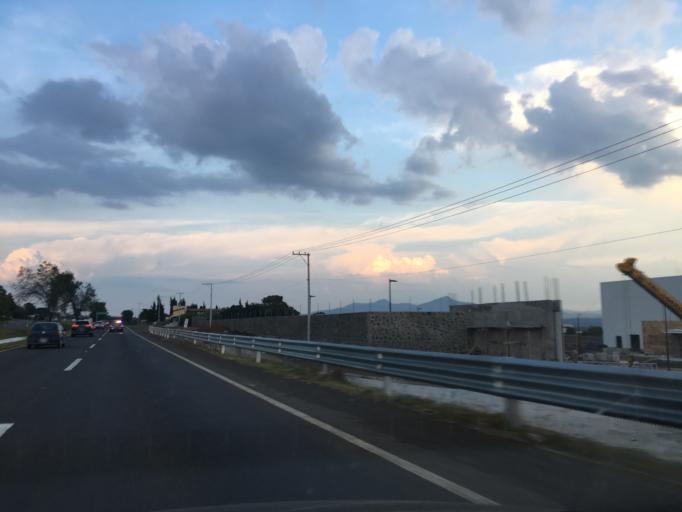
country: MX
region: Michoacan
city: Acuitzio del Canje
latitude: 19.5731
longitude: -101.3172
